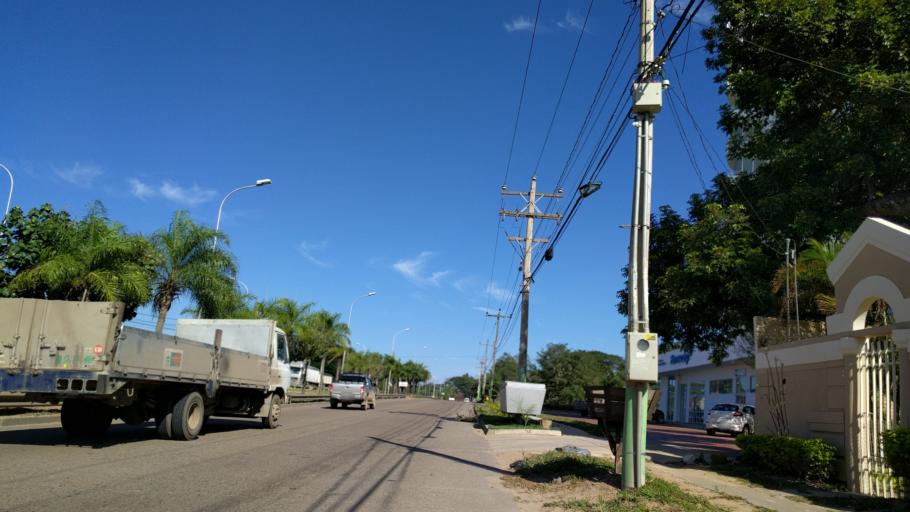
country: BO
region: Santa Cruz
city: Santa Cruz de la Sierra
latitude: -17.7993
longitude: -63.2201
